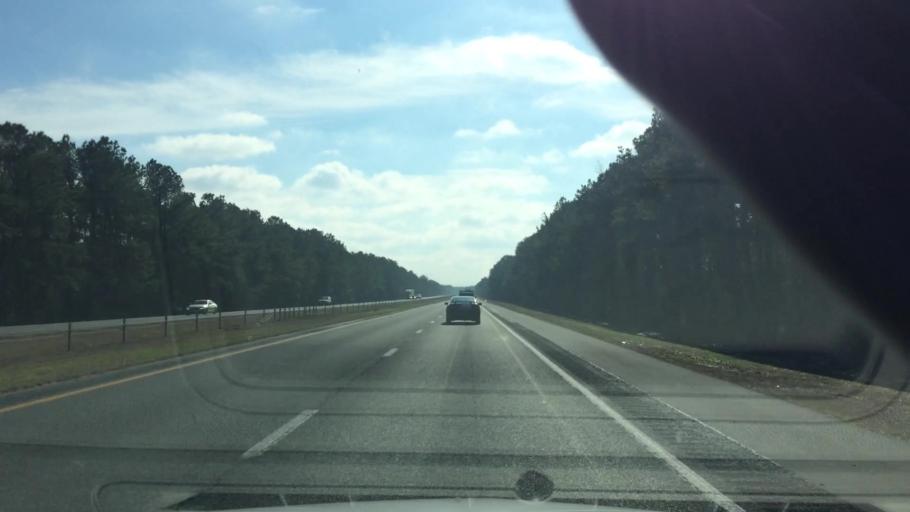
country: US
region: North Carolina
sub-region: Duplin County
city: Wallace
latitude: 34.7281
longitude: -77.9448
